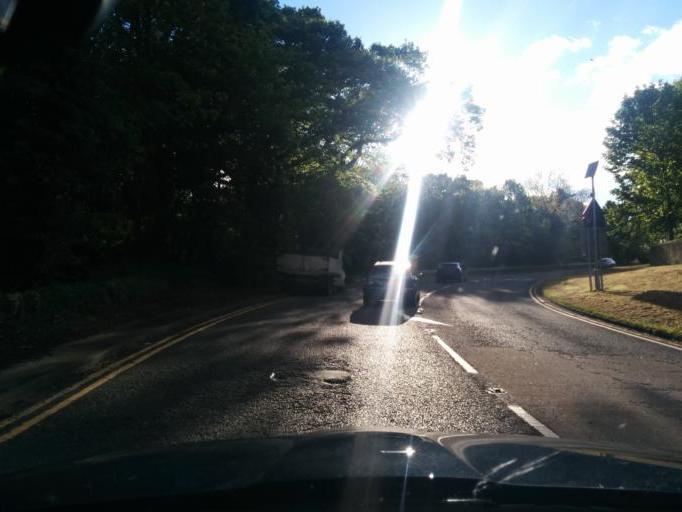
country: GB
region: England
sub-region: Northumberland
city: Bedlington
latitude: 55.1138
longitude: -1.6216
